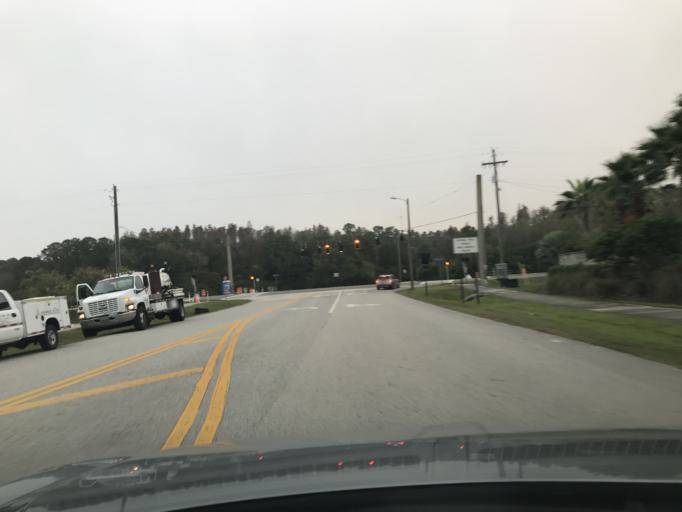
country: US
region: Florida
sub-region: Pinellas County
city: Oldsmar
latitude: 28.0512
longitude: -82.6680
